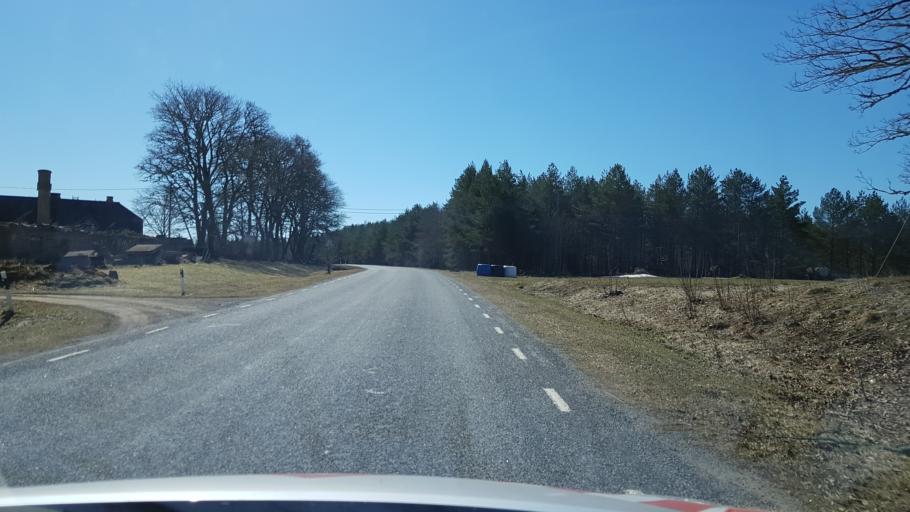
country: EE
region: Laeaene-Virumaa
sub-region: Haljala vald
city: Haljala
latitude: 59.5163
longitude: 26.2305
